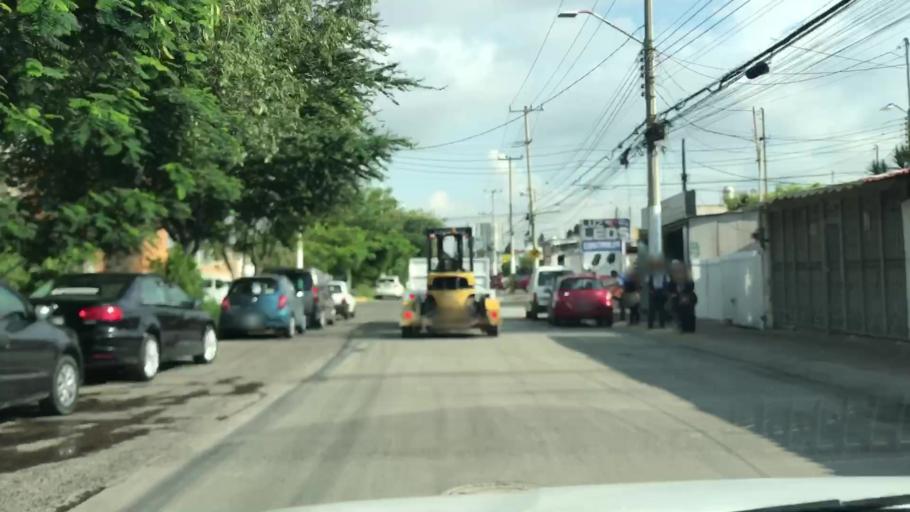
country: MX
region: Jalisco
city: Guadalajara
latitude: 20.6479
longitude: -103.4326
